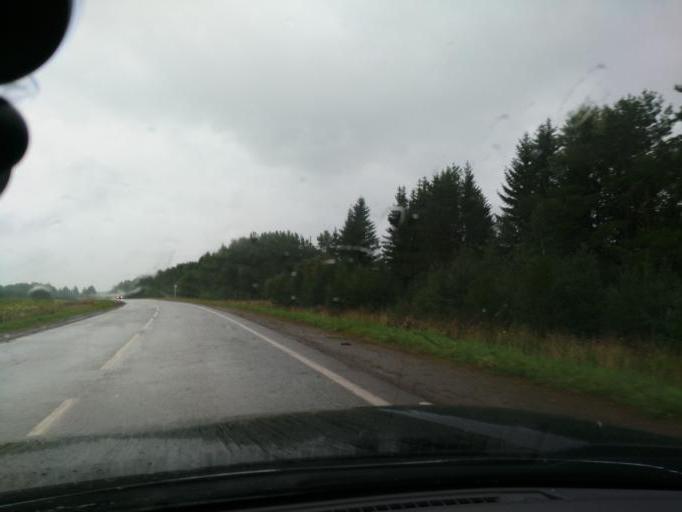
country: RU
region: Perm
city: Osa
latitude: 57.2895
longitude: 55.5960
